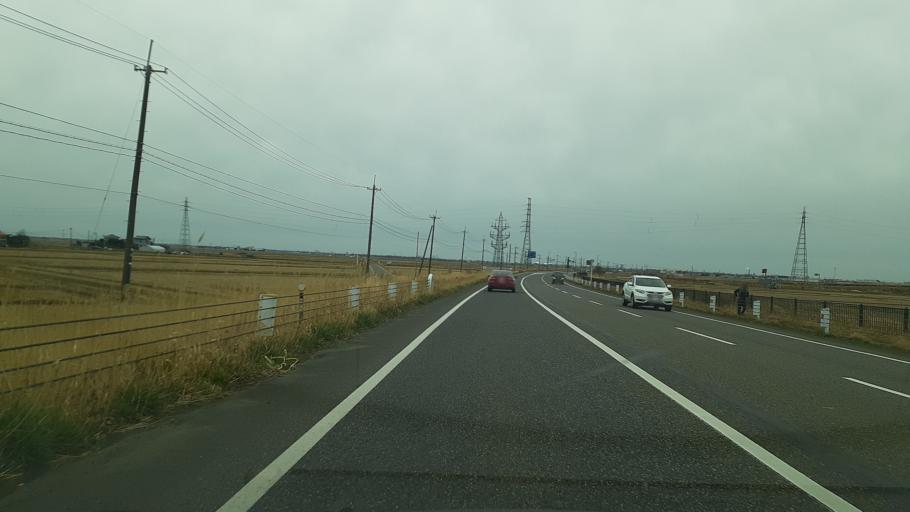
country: JP
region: Niigata
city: Niitsu-honcho
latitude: 37.8001
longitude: 139.1042
